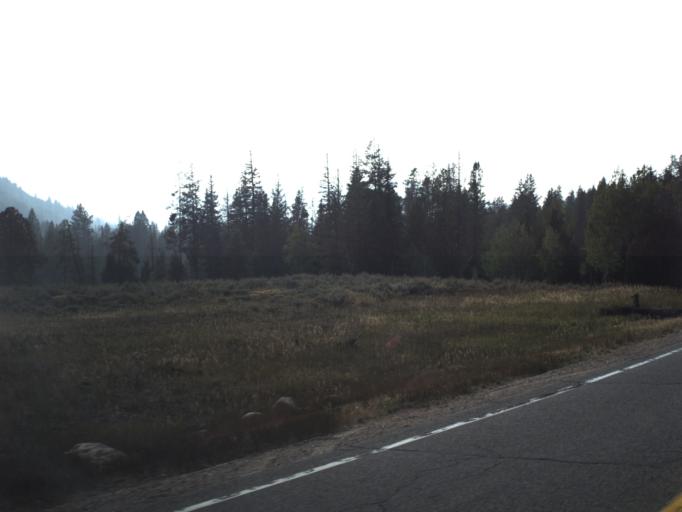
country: US
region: Utah
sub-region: Summit County
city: Francis
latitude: 40.5937
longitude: -111.0726
